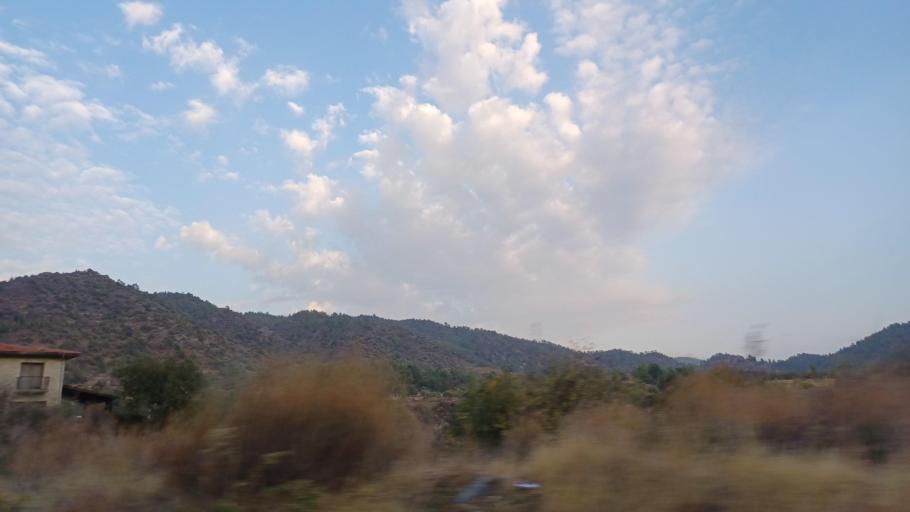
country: CY
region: Limassol
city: Pelendri
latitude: 34.8246
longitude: 32.9645
